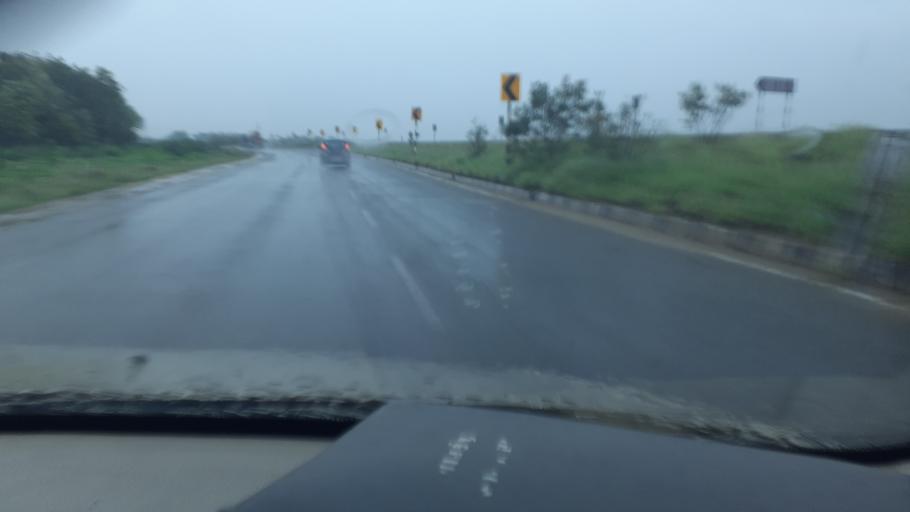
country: IN
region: Tamil Nadu
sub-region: Virudhunagar
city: Sattur
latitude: 9.4156
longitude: 77.9158
